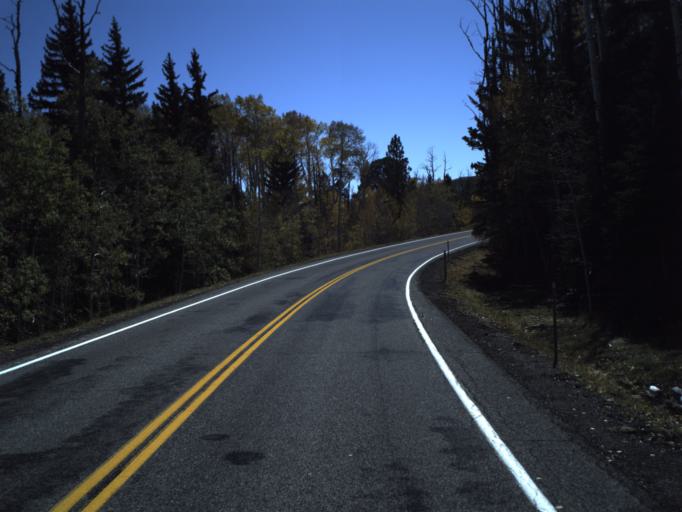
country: US
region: Utah
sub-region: Wayne County
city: Loa
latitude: 38.0854
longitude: -111.3373
